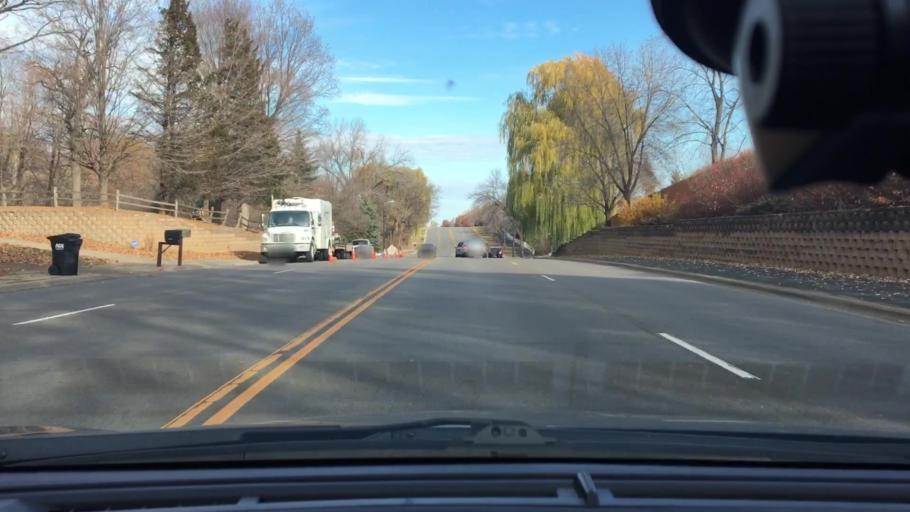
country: US
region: Minnesota
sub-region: Hennepin County
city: Maple Grove
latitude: 45.1101
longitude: -93.4922
